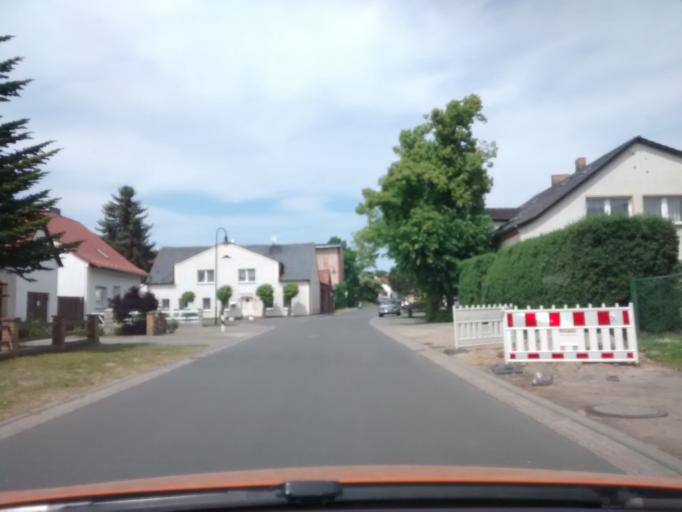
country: DE
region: Brandenburg
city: Ihlow
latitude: 51.8893
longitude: 13.3048
